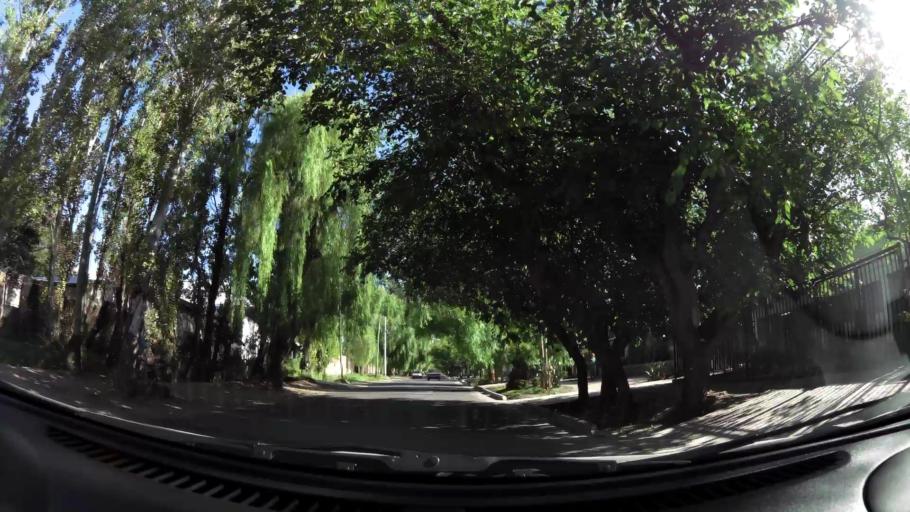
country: AR
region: Mendoza
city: Mendoza
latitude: -32.9034
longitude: -68.8055
